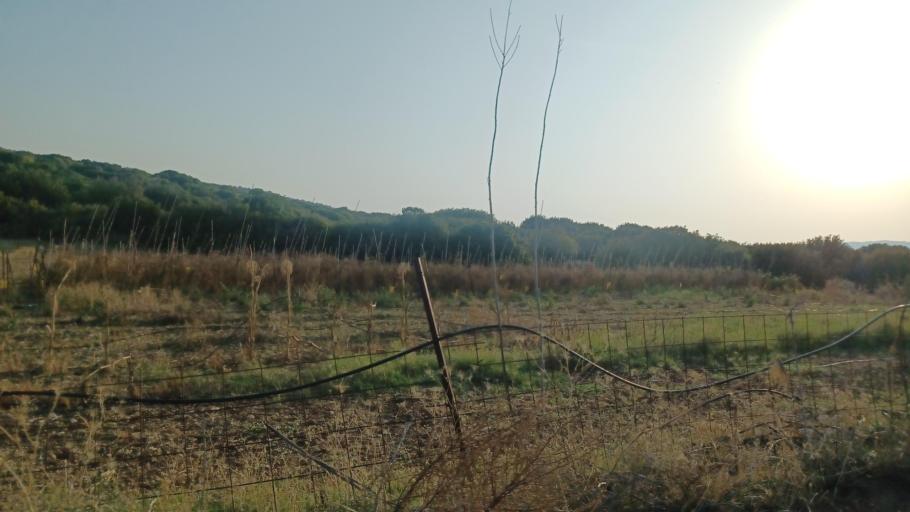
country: CY
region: Pafos
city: Polis
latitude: 34.9635
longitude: 32.4866
